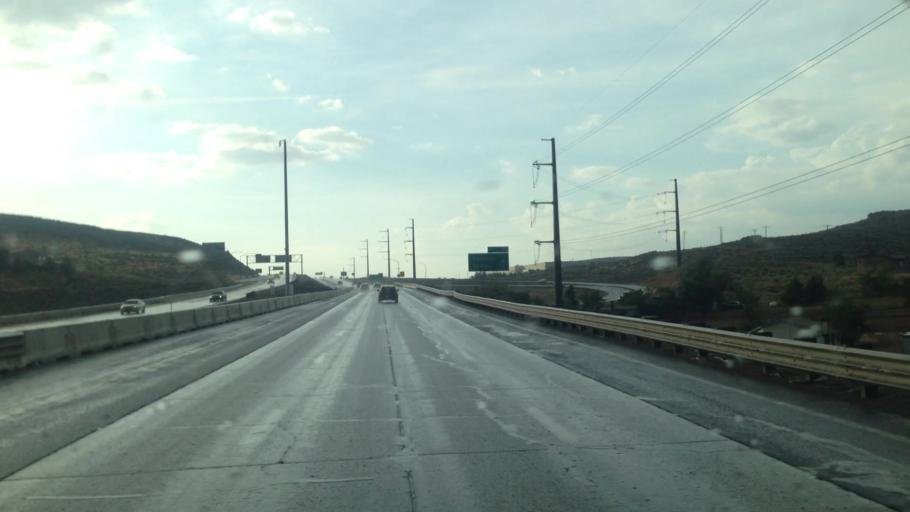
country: US
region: Nevada
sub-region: Washoe County
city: Golden Valley
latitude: 39.5884
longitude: -119.8250
